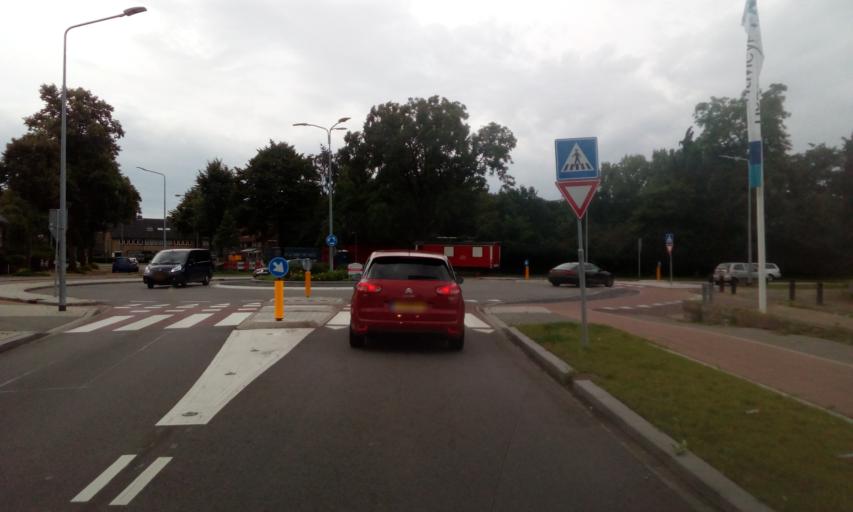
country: NL
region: North Holland
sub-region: Gemeente Wijdemeren
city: Nieuw-Loosdrecht
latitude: 52.2210
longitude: 5.1513
